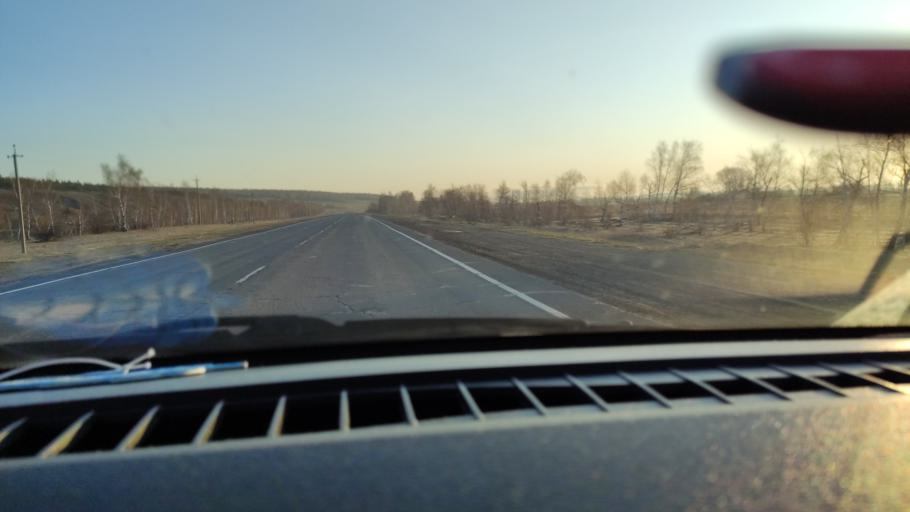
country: RU
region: Saratov
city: Sinodskoye
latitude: 52.0588
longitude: 46.7605
